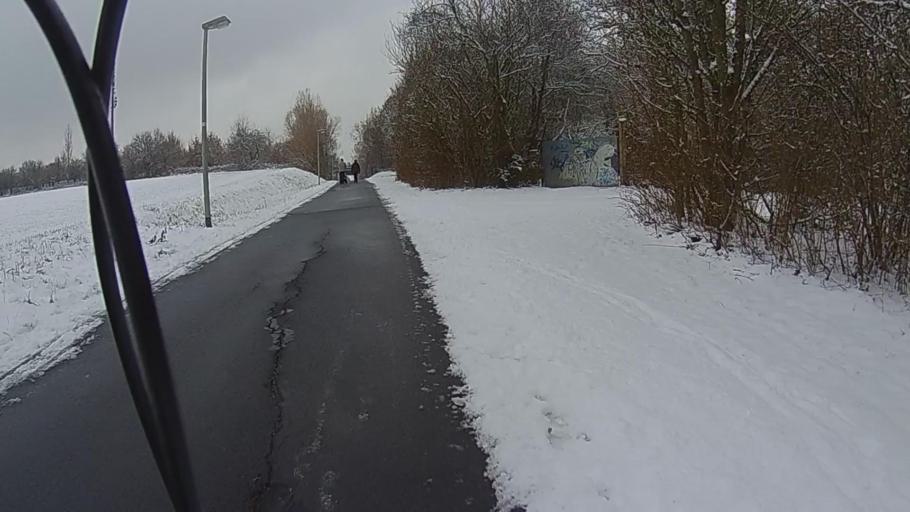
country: DE
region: Hesse
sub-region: Regierungsbezirk Darmstadt
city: Oberursel
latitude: 50.1904
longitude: 8.5760
